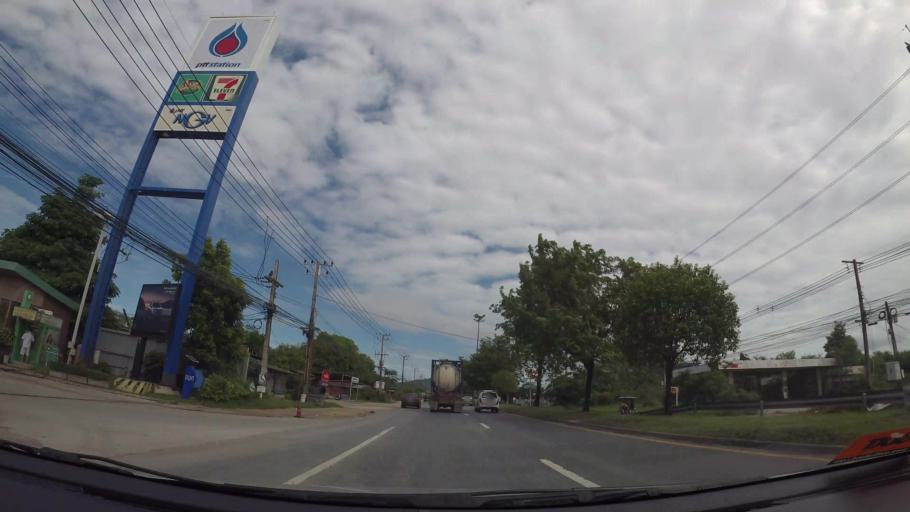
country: TH
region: Rayong
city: Ban Chang
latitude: 12.7380
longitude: 101.1260
